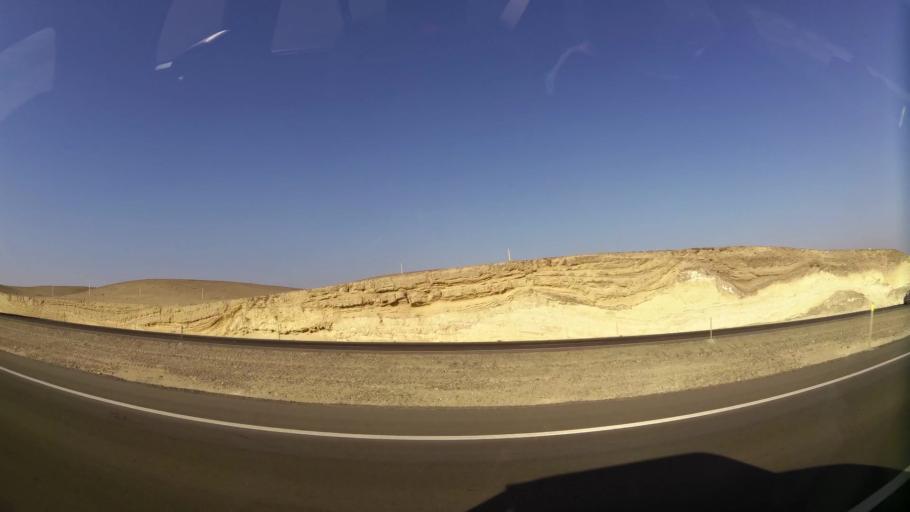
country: PE
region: Ica
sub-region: Provincia de Pisco
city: San Clemente
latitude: -13.6520
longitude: -76.1738
